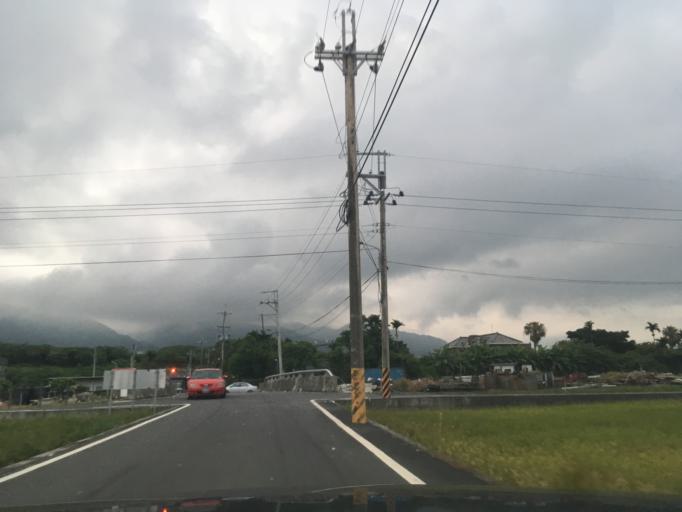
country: TW
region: Taiwan
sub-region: Yilan
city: Yilan
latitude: 24.8210
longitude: 121.7864
